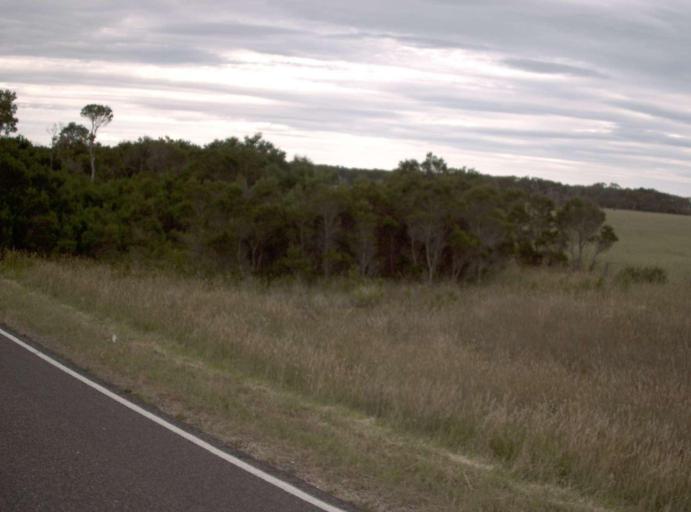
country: AU
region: Victoria
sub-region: East Gippsland
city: Bairnsdale
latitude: -37.9867
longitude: 147.3998
